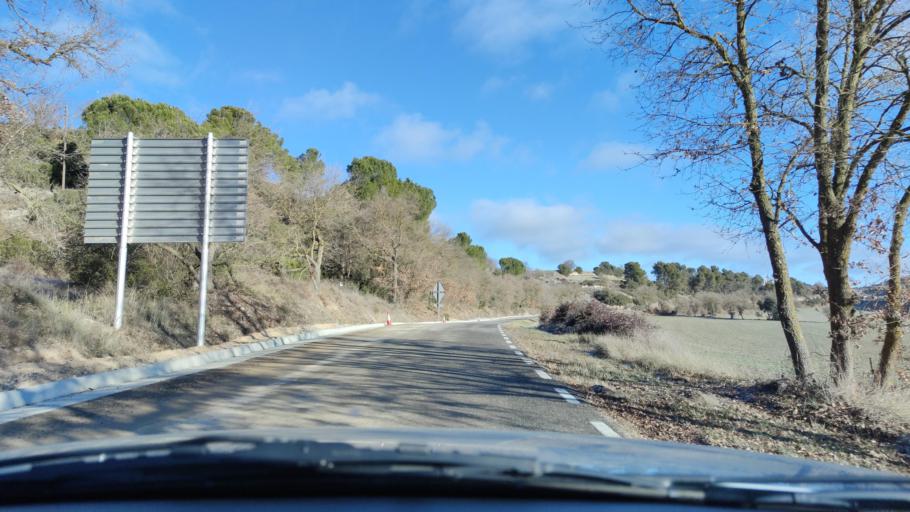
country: ES
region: Catalonia
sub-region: Provincia de Barcelona
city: Pujalt
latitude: 41.6976
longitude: 1.3455
